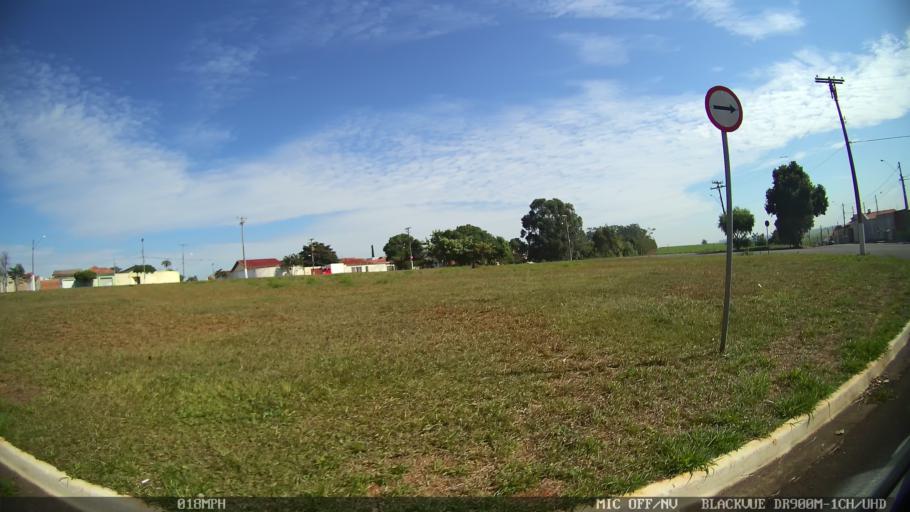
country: BR
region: Sao Paulo
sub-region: Santa Barbara D'Oeste
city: Santa Barbara d'Oeste
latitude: -22.7429
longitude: -47.4225
